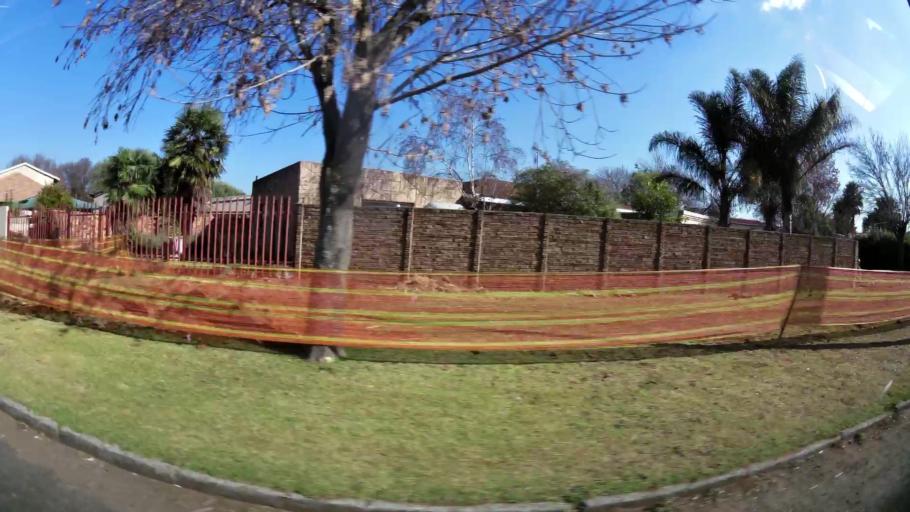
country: ZA
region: Gauteng
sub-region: Ekurhuleni Metropolitan Municipality
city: Benoni
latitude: -26.1503
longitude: 28.3094
